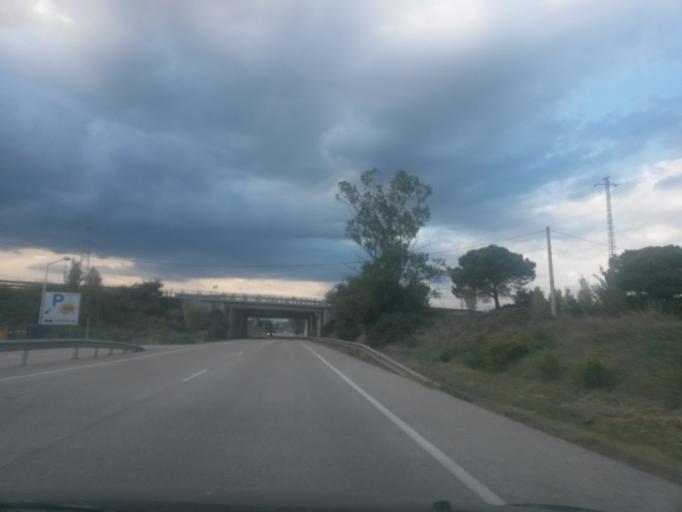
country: ES
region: Catalonia
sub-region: Provincia de Girona
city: Riudellots de la Selva
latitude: 41.8946
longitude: 2.7764
